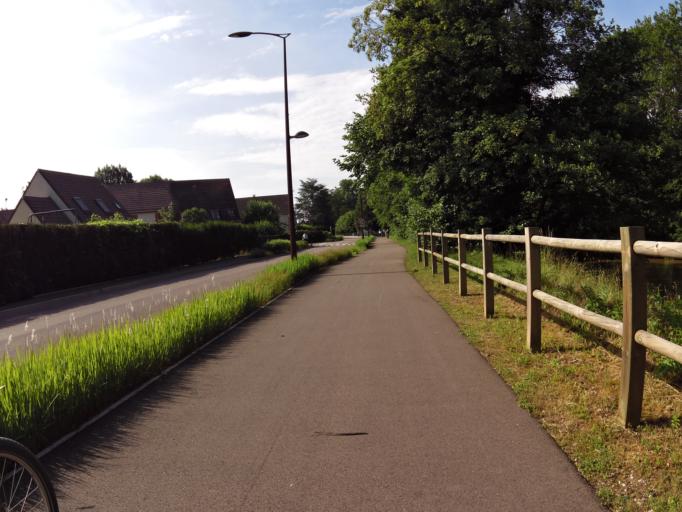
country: FR
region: Champagne-Ardenne
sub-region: Departement de l'Aube
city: Saint-Julien-les-Villas
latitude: 48.2758
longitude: 4.1001
